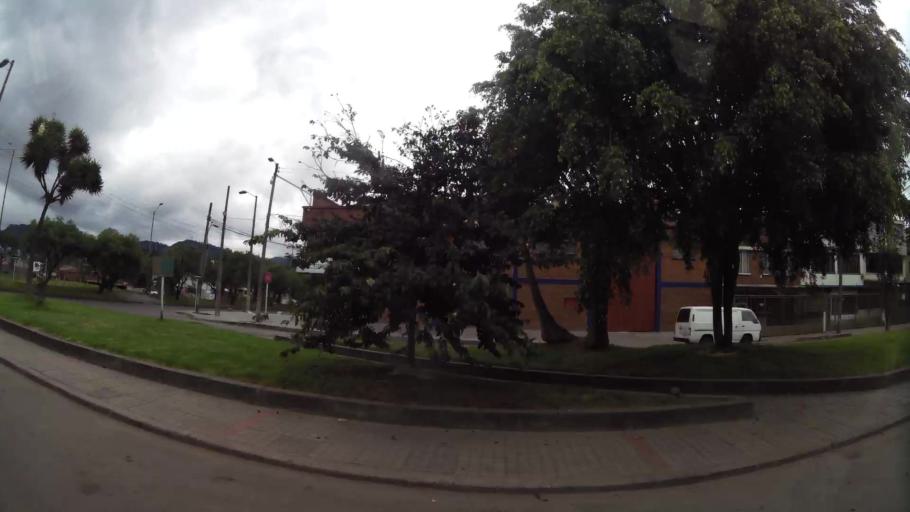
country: CO
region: Bogota D.C.
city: Bogota
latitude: 4.6098
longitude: -74.1027
